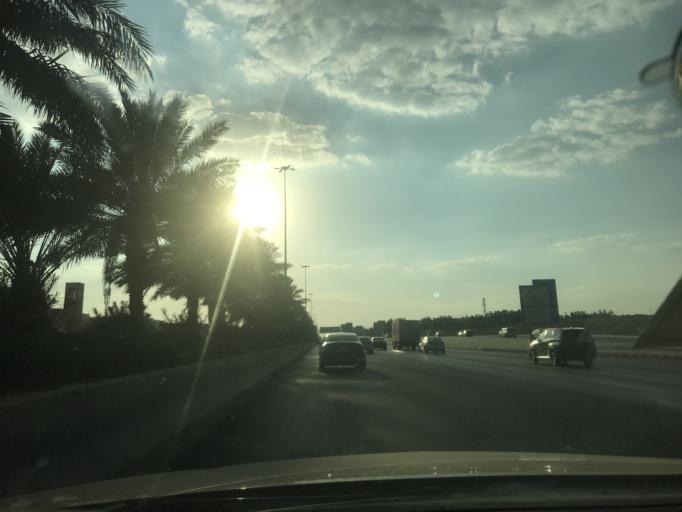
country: SA
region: Ar Riyad
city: Riyadh
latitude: 24.7515
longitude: 46.6244
